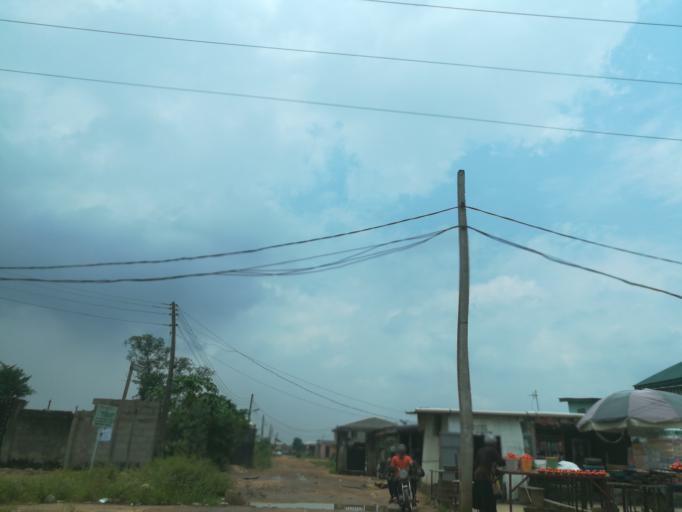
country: NG
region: Lagos
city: Ikorodu
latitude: 6.6175
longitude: 3.5644
